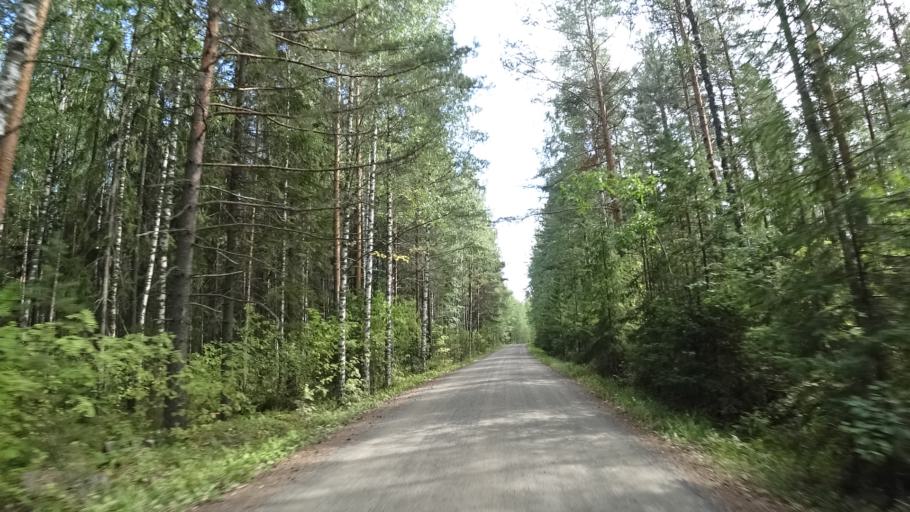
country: FI
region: North Karelia
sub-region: Joensuu
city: Pyhaeselkae
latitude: 62.3864
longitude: 29.7959
